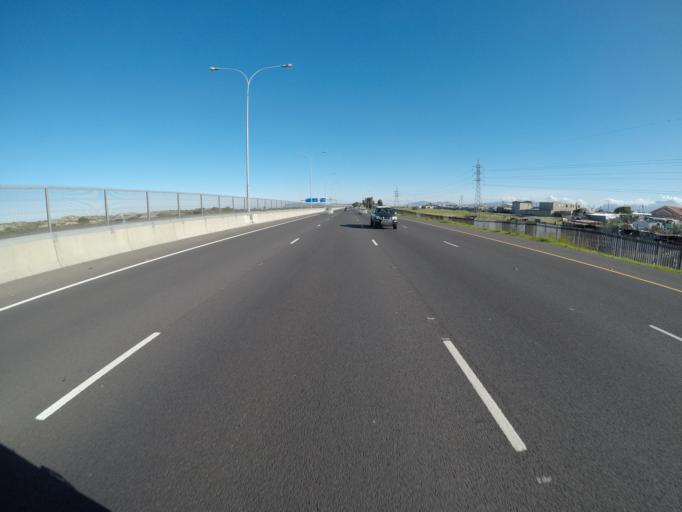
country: ZA
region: Western Cape
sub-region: City of Cape Town
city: Lansdowne
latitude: -33.9927
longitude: 18.6418
